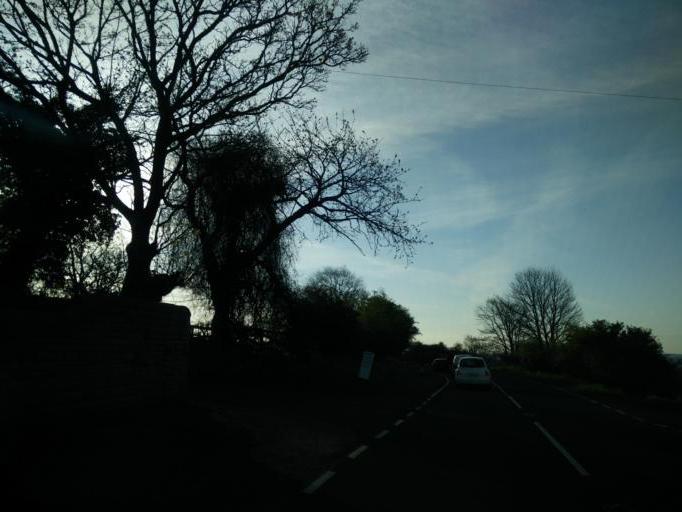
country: GB
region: England
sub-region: County Durham
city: Crook
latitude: 54.6763
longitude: -1.7211
